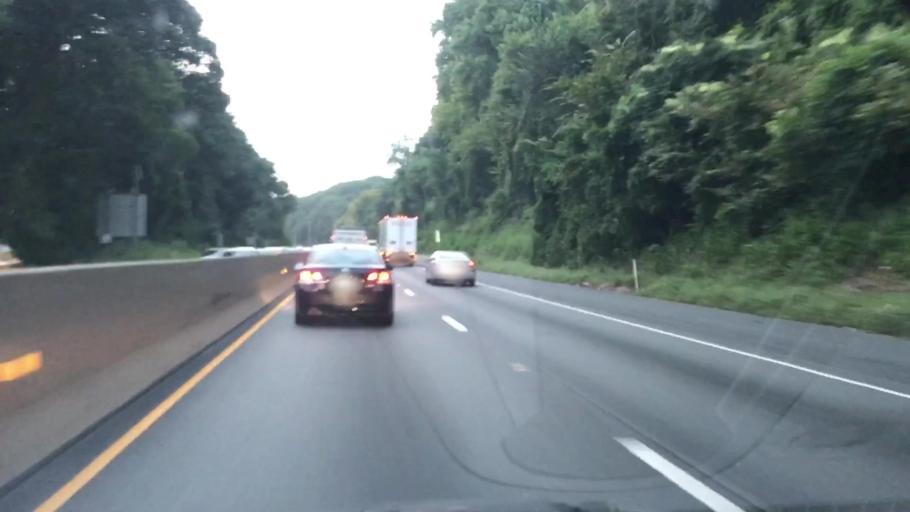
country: US
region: Pennsylvania
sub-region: Montgomery County
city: Narberth
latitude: 40.0491
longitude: -75.2618
